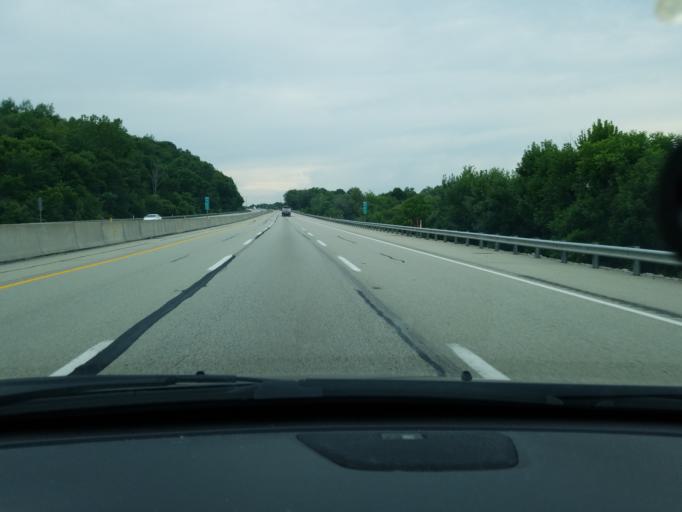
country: US
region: Pennsylvania
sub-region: Lawrence County
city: Bessemer
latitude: 40.9009
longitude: -80.4835
